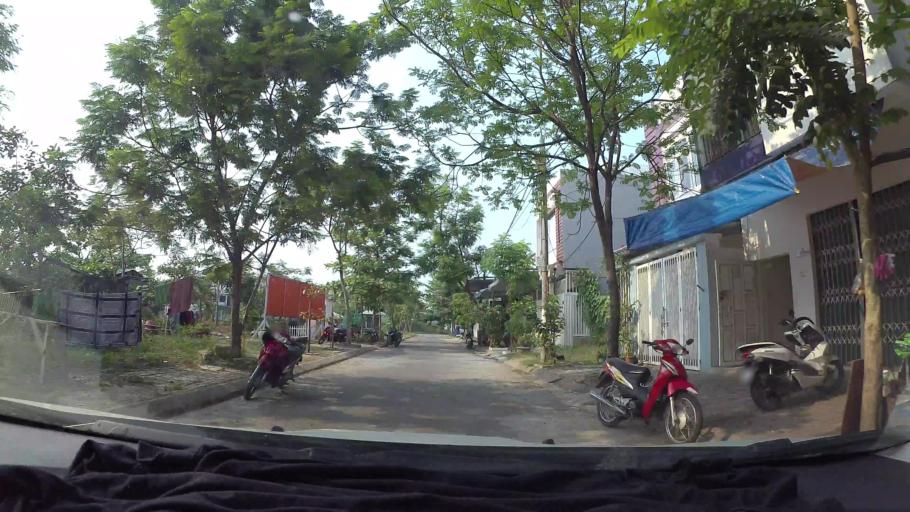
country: VN
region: Da Nang
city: Lien Chieu
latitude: 16.0525
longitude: 108.1657
